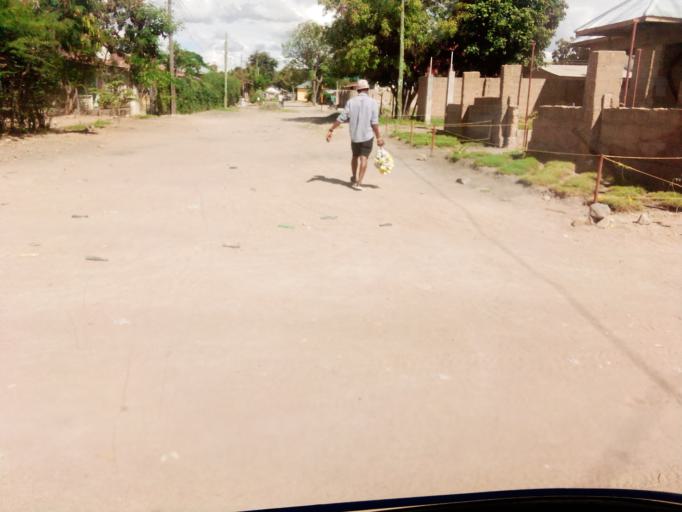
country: TZ
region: Dodoma
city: Dodoma
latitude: -6.1765
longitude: 35.7559
